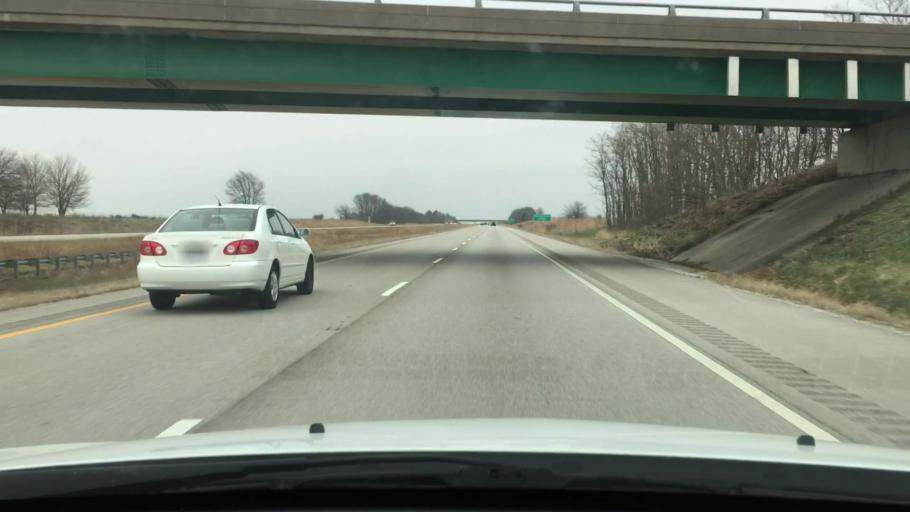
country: US
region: Illinois
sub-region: Sangamon County
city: New Berlin
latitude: 39.7399
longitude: -89.9386
